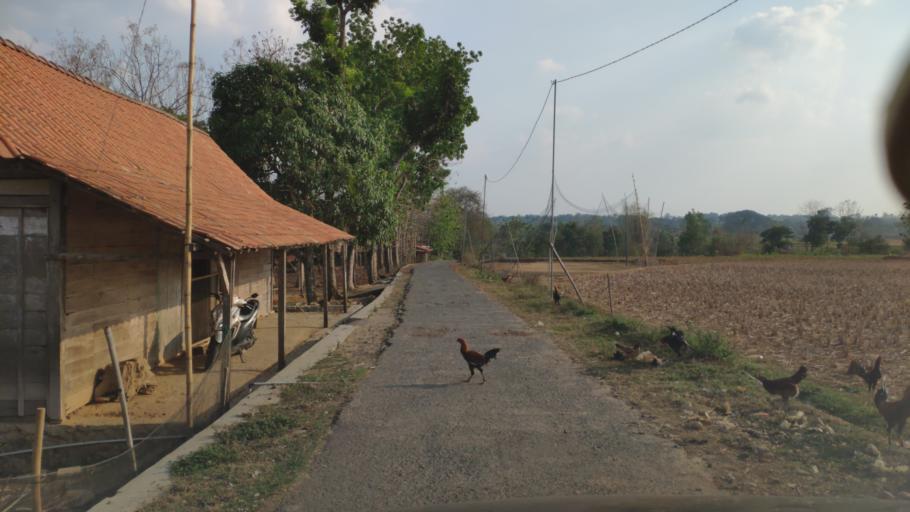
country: ID
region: Central Java
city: Guyangan
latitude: -6.9557
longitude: 111.1245
